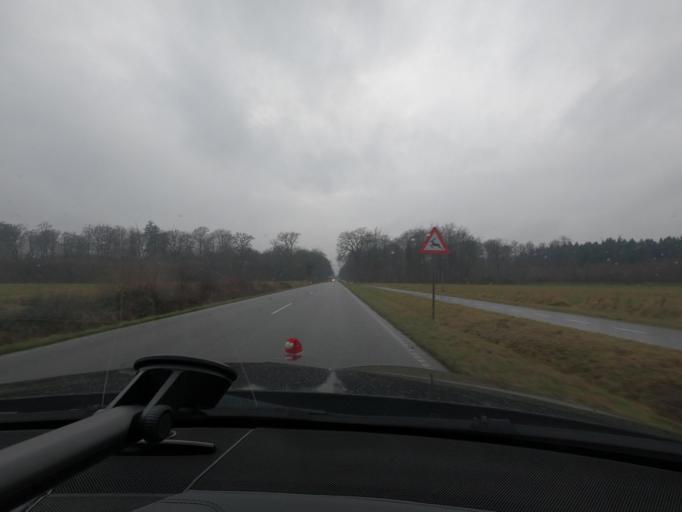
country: DK
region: South Denmark
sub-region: Sonderborg Kommune
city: Sonderborg
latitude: 54.9064
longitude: 9.8416
